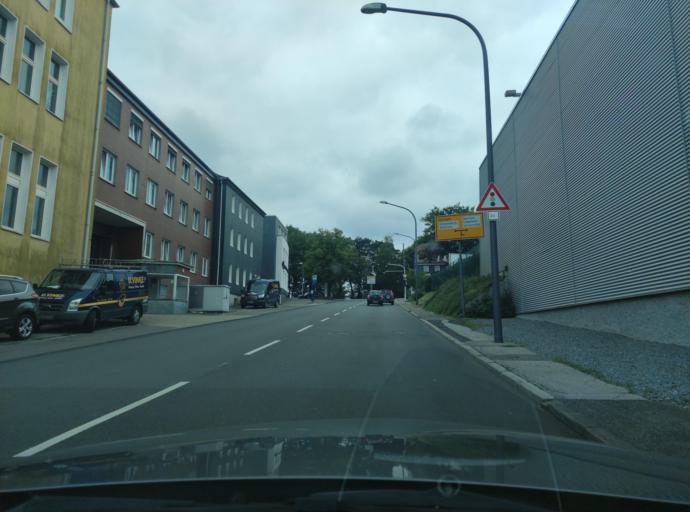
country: DE
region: North Rhine-Westphalia
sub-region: Regierungsbezirk Dusseldorf
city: Remscheid
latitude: 51.2141
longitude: 7.1471
